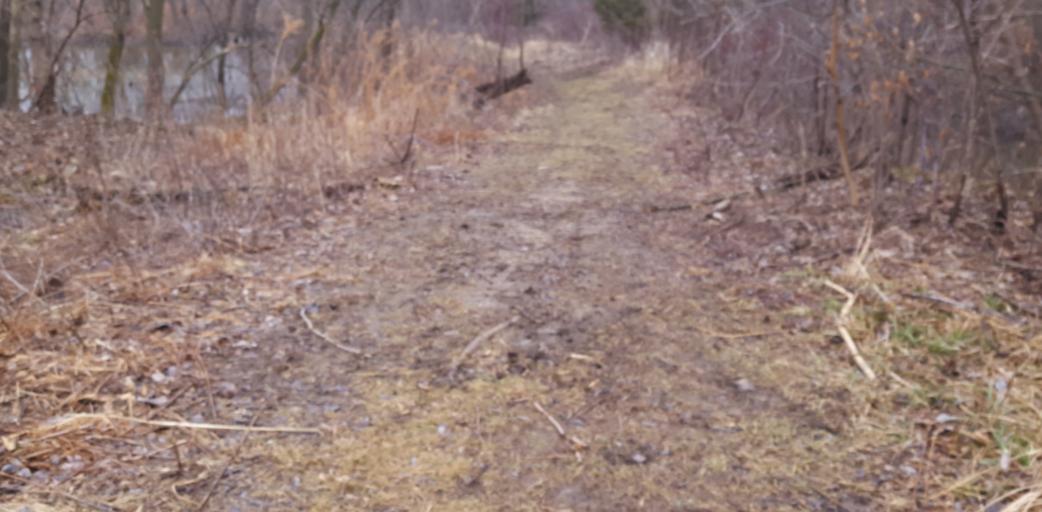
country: US
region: Illinois
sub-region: Cook County
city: Northfield
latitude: 42.0926
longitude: -87.8066
